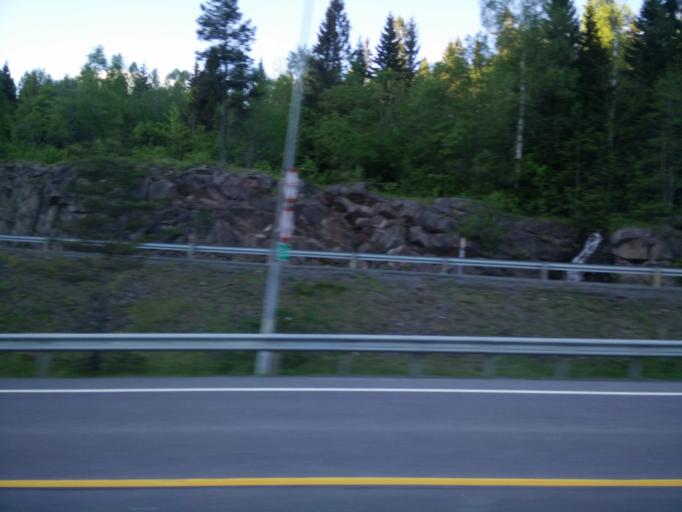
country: NO
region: Buskerud
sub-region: Hole
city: Vik
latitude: 59.9808
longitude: 10.3147
